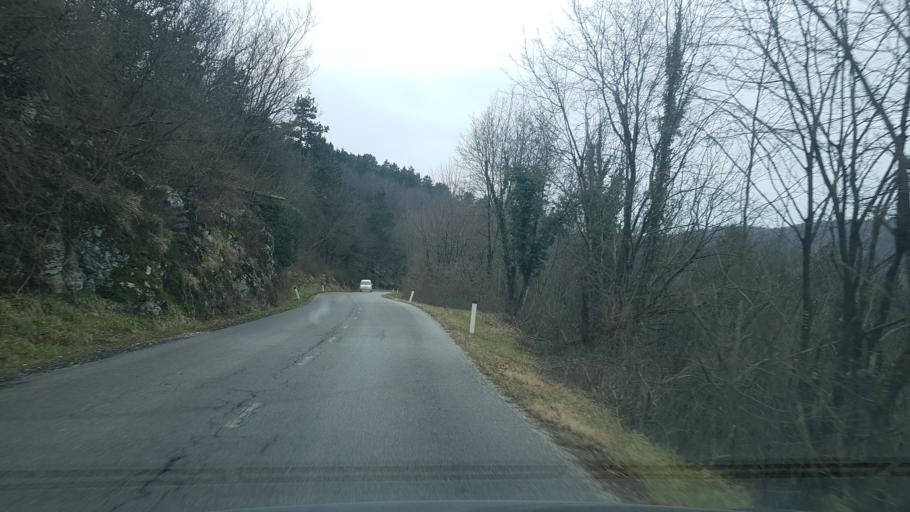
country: SI
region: Kanal
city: Deskle
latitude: 46.0379
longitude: 13.6720
